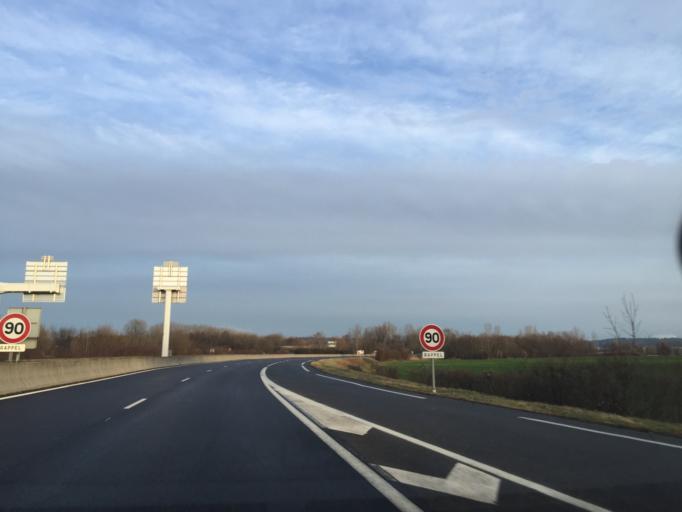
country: FR
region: Rhone-Alpes
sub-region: Departement de l'Isere
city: Saint-Alban-de-Roche
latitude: 45.6097
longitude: 5.2223
